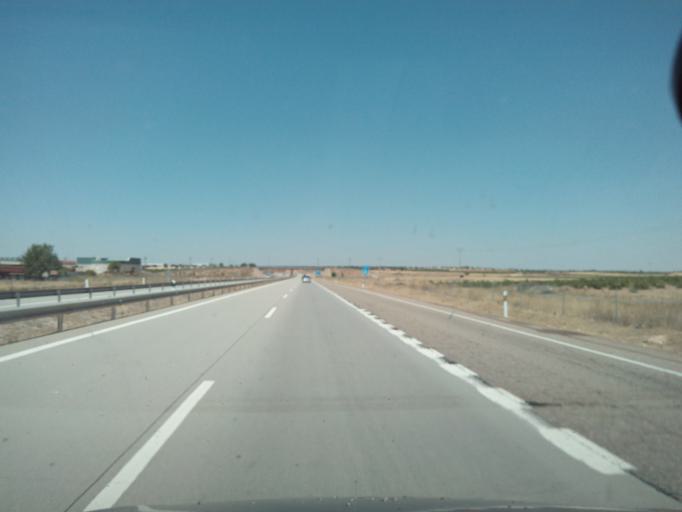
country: ES
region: Castille-La Mancha
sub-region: Province of Toledo
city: Dosbarrios
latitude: 39.8791
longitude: -3.4737
